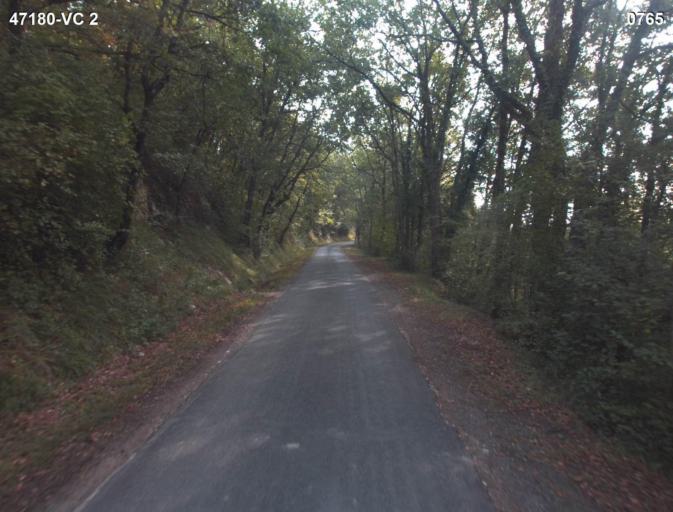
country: FR
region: Aquitaine
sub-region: Departement du Lot-et-Garonne
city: Nerac
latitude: 44.1654
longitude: 0.4296
